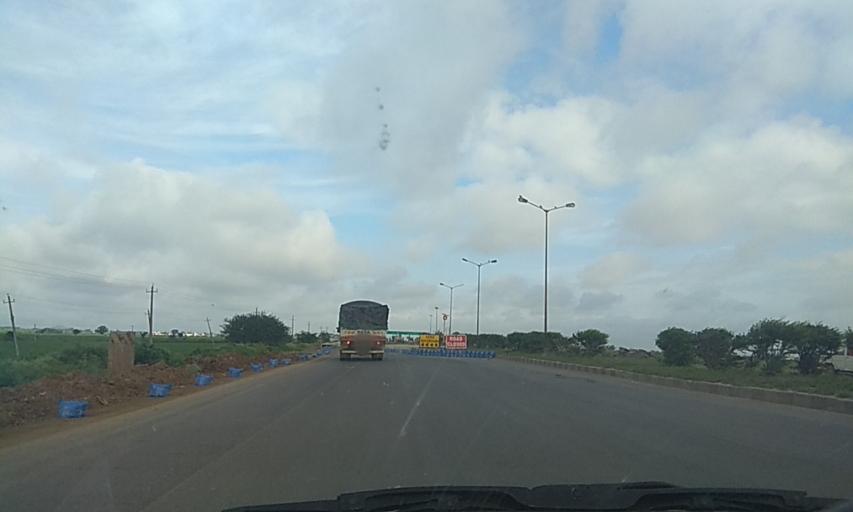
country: IN
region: Karnataka
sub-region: Haveri
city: Savanur
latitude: 14.9063
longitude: 75.2834
